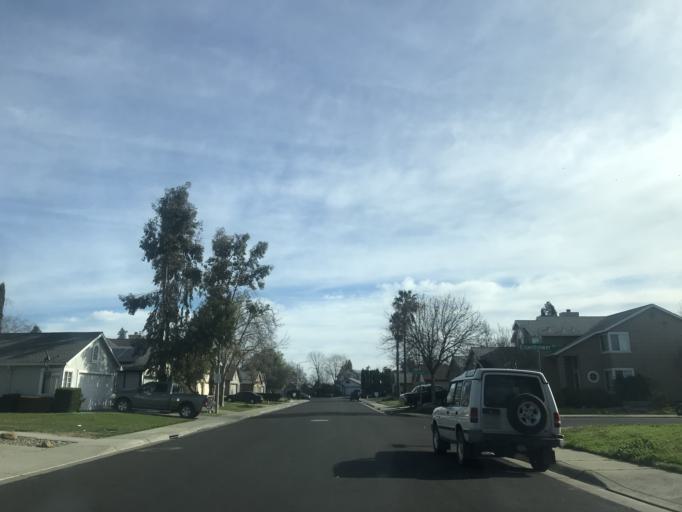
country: US
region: California
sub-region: Yolo County
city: Woodland
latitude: 38.6602
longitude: -121.7551
